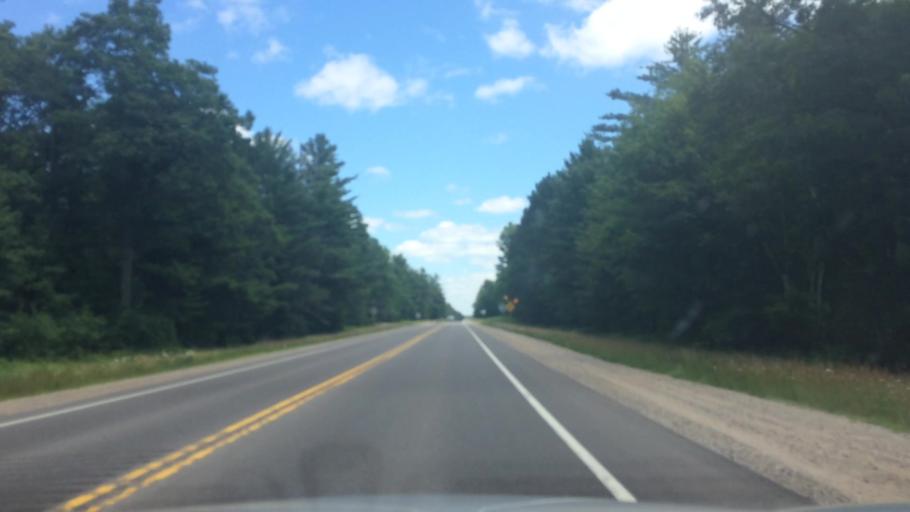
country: US
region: Wisconsin
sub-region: Vilas County
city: Lac du Flambeau
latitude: 45.9833
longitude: -89.6973
